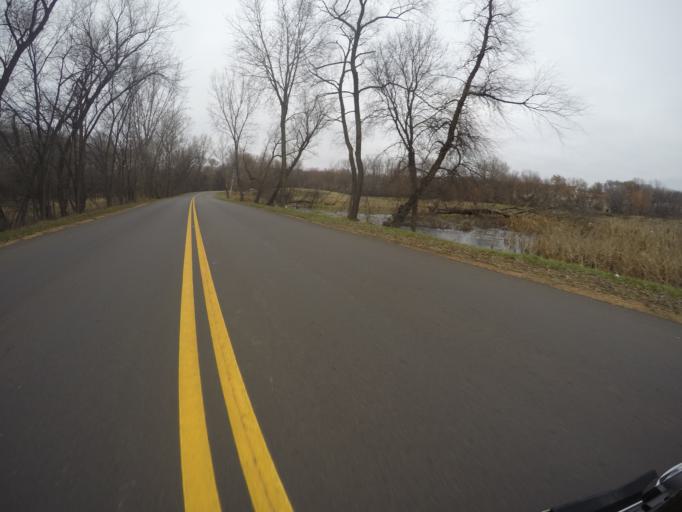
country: US
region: Minnesota
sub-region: Hennepin County
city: Eden Prairie
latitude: 44.8722
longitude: -93.4692
